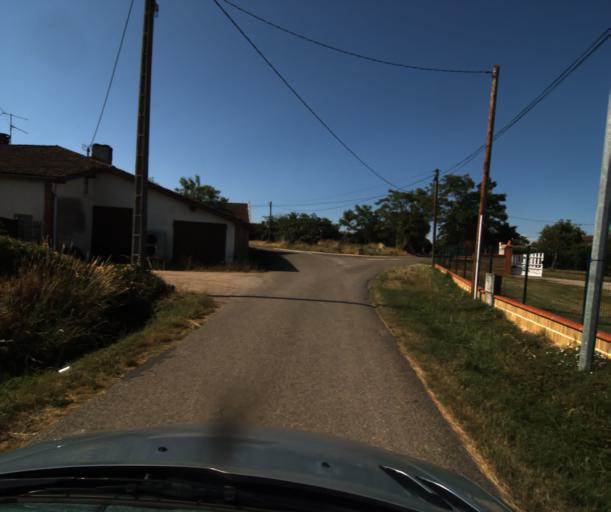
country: FR
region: Midi-Pyrenees
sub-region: Departement du Tarn-et-Garonne
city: Finhan
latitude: 43.9154
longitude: 1.2667
